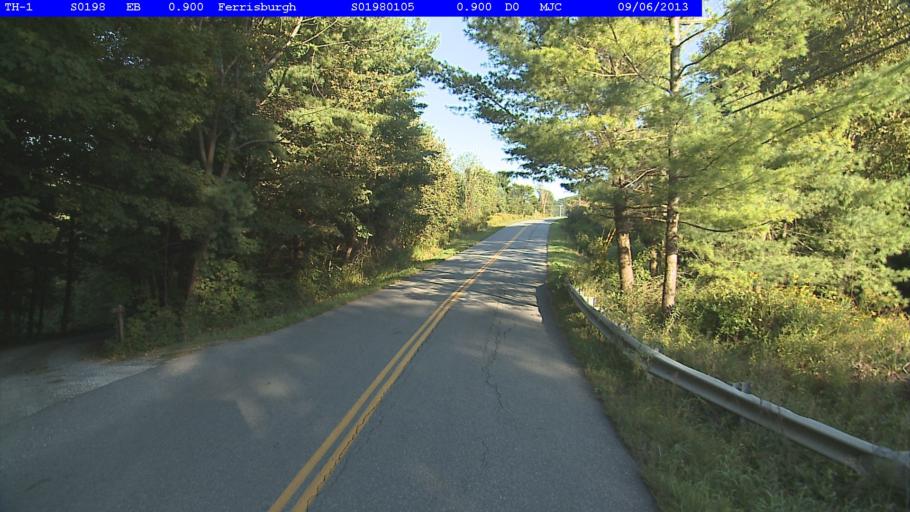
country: US
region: Vermont
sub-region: Addison County
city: Vergennes
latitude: 44.2592
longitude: -73.2102
